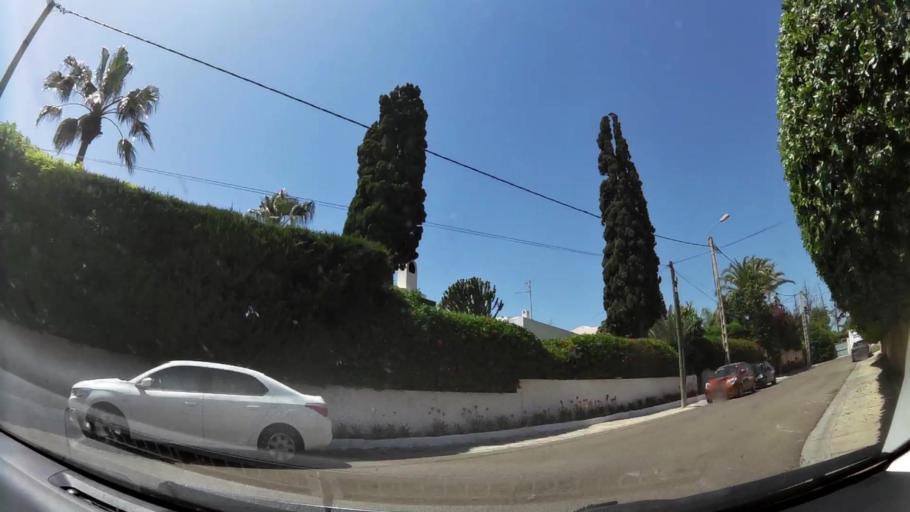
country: MA
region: Souss-Massa-Draa
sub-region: Agadir-Ida-ou-Tnan
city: Agadir
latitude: 30.4299
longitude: -9.5985
